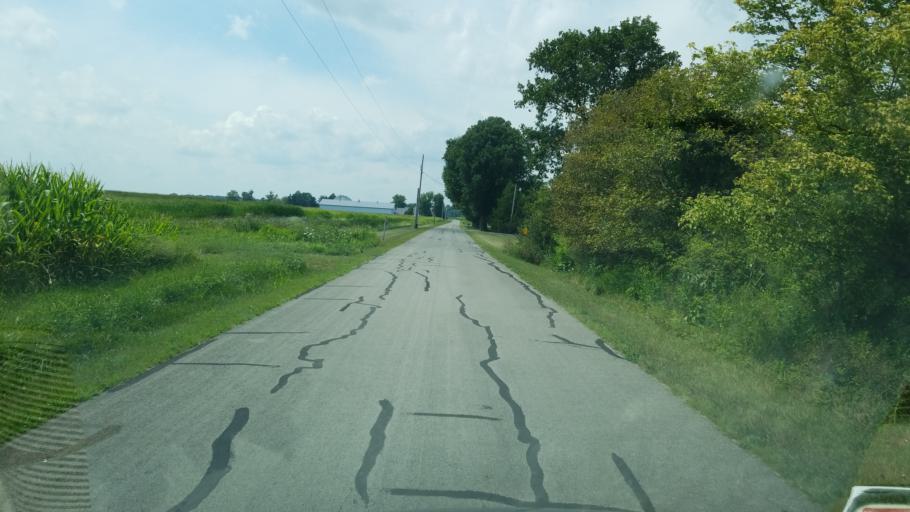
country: US
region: Ohio
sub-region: Hancock County
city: Arlington
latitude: 40.8848
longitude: -83.7396
